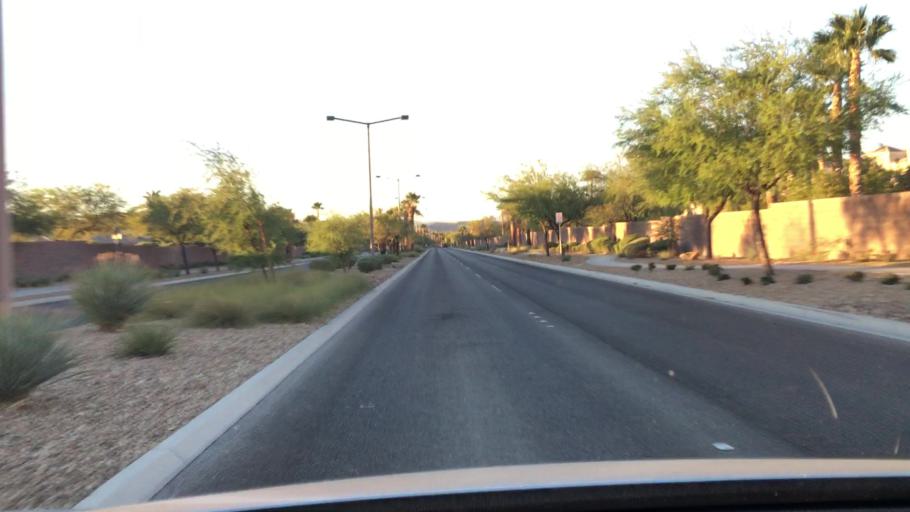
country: US
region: Nevada
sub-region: Clark County
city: Summerlin South
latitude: 36.1397
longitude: -115.3425
